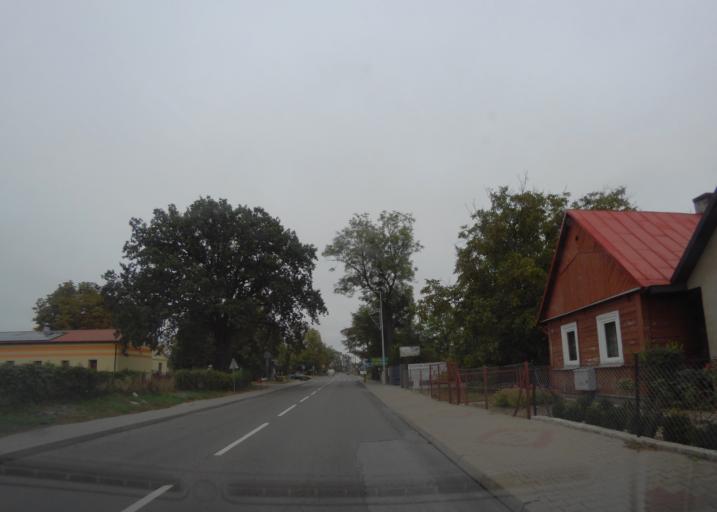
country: PL
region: Lublin Voivodeship
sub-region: Powiat chelmski
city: Rejowiec
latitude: 51.0937
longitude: 23.2832
